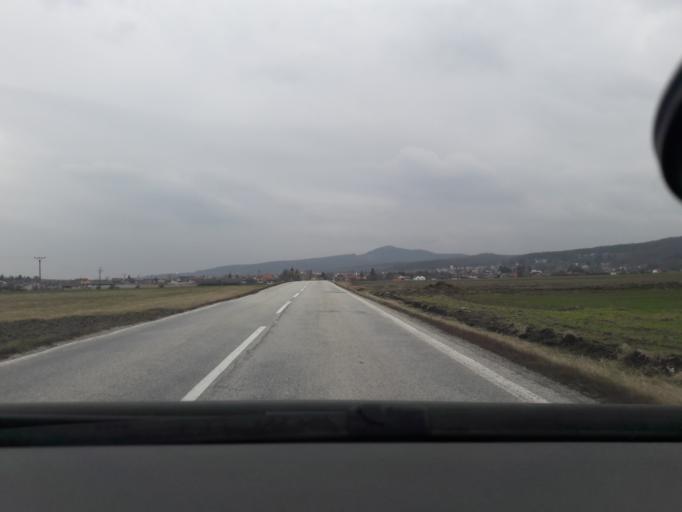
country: SK
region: Bratislavsky
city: Modra
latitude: 48.4044
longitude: 17.3747
